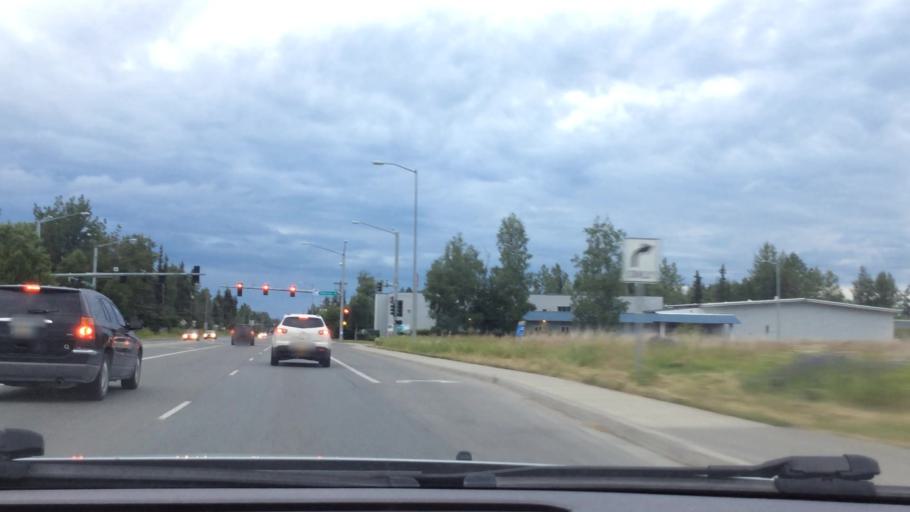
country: US
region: Alaska
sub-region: Anchorage Municipality
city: Elmendorf Air Force Base
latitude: 61.2098
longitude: -149.7465
